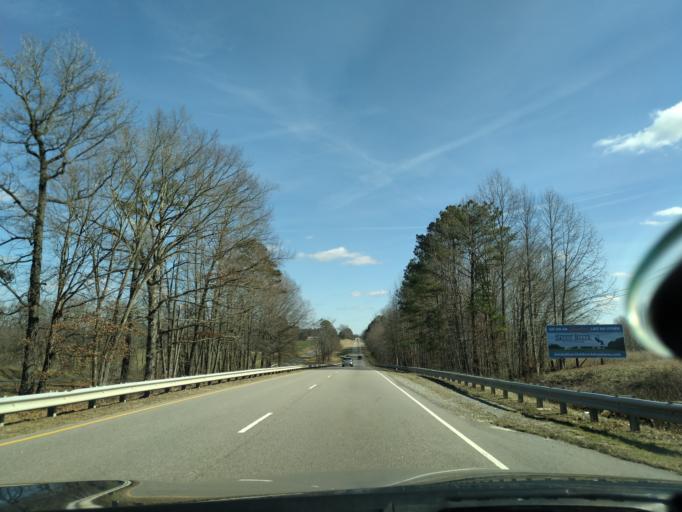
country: US
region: Virginia
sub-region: Nottoway County
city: Crewe
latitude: 37.1898
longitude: -78.1696
